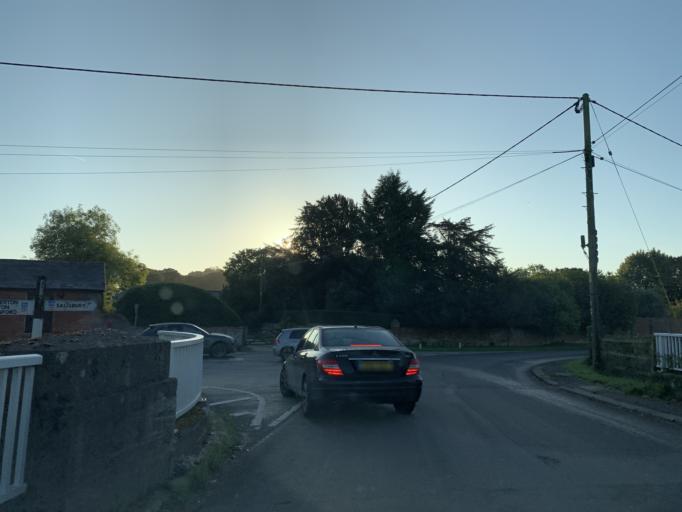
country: GB
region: England
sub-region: Wiltshire
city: Woodford
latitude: 51.0956
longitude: -1.8167
